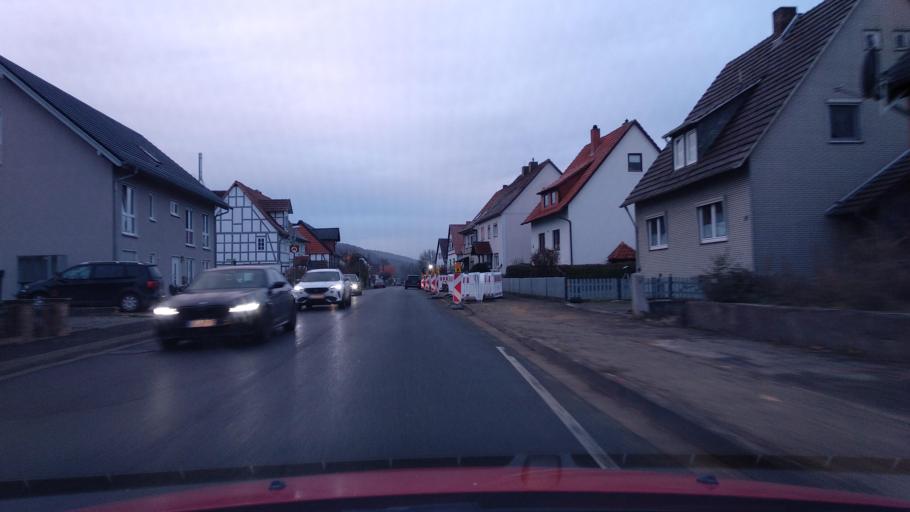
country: DE
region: Hesse
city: Liebenau
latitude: 51.4439
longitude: 9.3034
